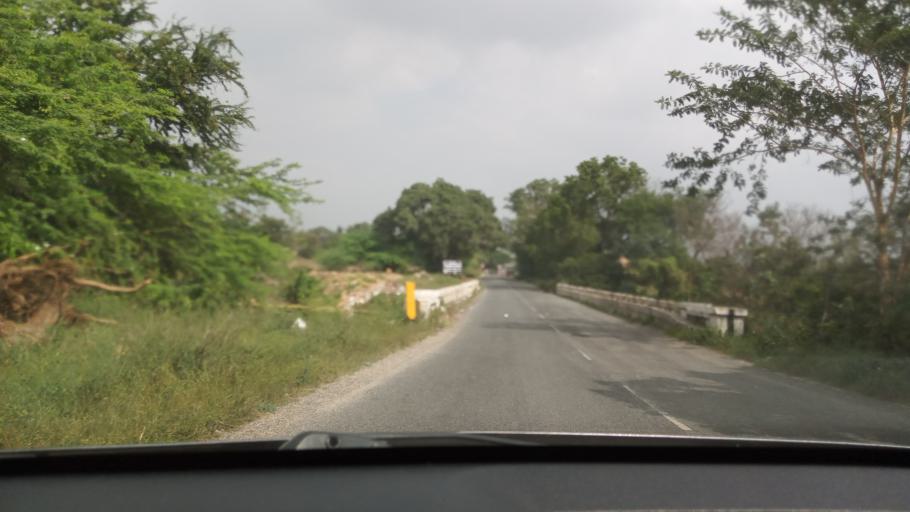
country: IN
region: Andhra Pradesh
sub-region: Chittoor
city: Madanapalle
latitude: 13.6518
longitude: 78.8229
